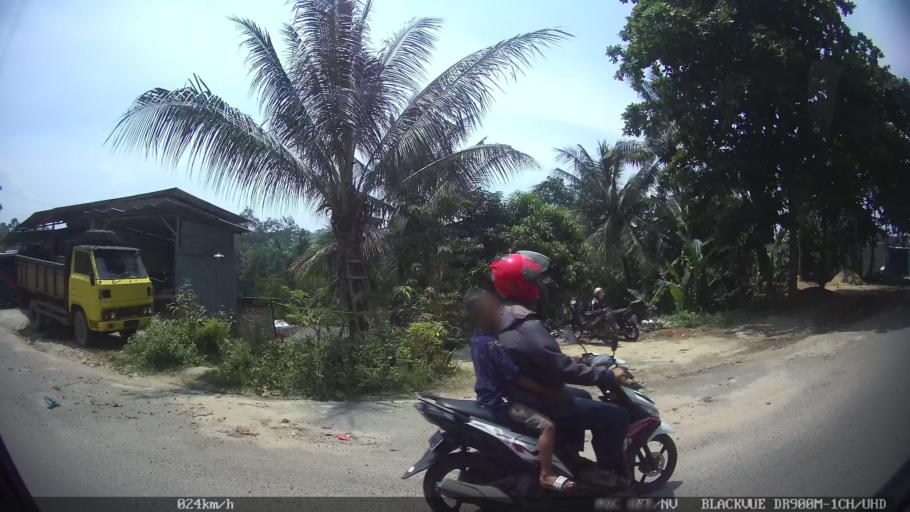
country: ID
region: Lampung
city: Bandarlampung
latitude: -5.4378
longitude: 105.2434
